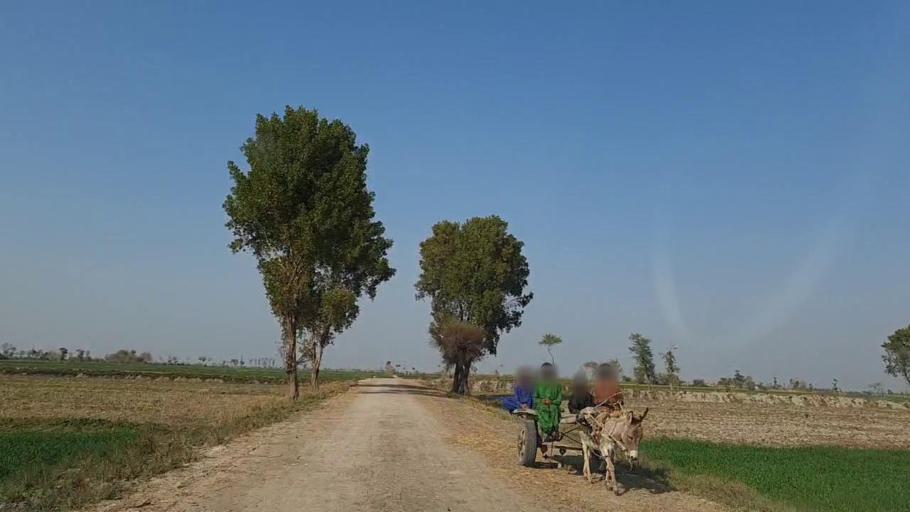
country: PK
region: Sindh
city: Daur
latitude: 26.4867
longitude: 68.2974
